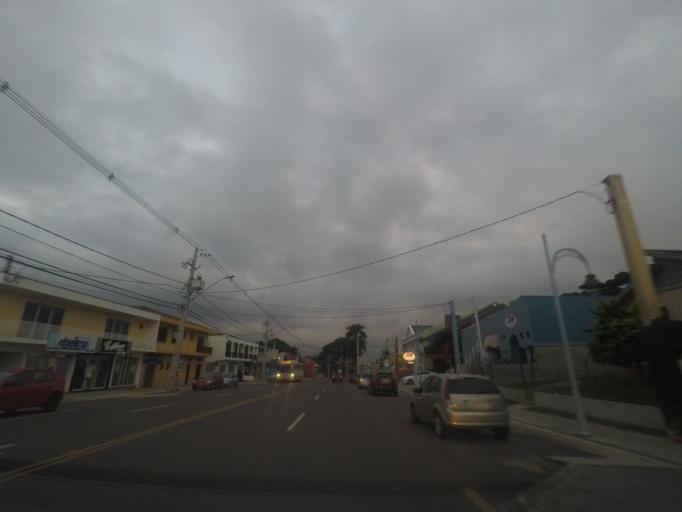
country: BR
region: Parana
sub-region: Curitiba
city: Curitiba
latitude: -25.3971
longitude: -49.3444
